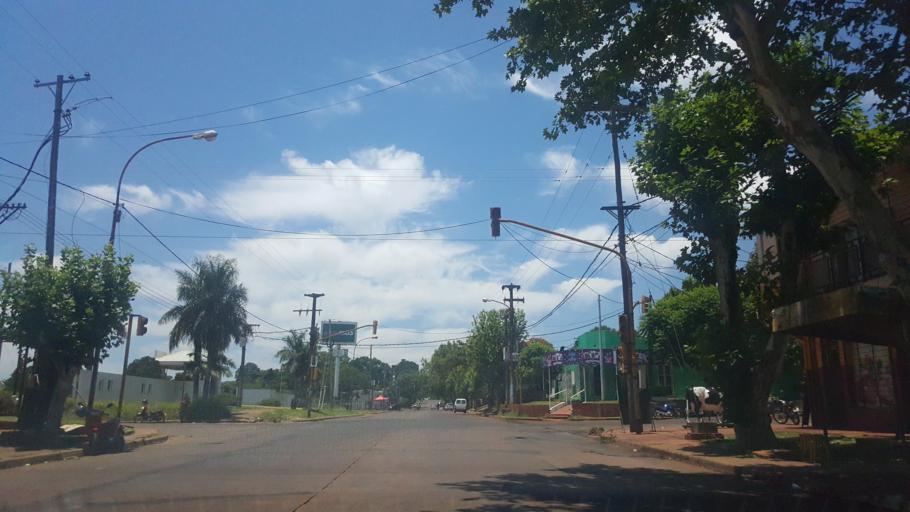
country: AR
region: Misiones
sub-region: Departamento de Capital
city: Posadas
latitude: -27.3676
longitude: -55.9285
